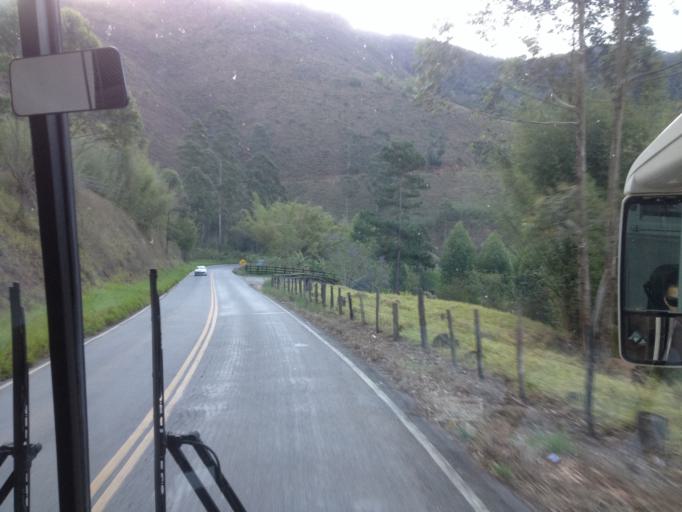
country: BR
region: Minas Gerais
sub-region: Juiz De Fora
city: Juiz de Fora
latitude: -21.6545
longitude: -43.3315
